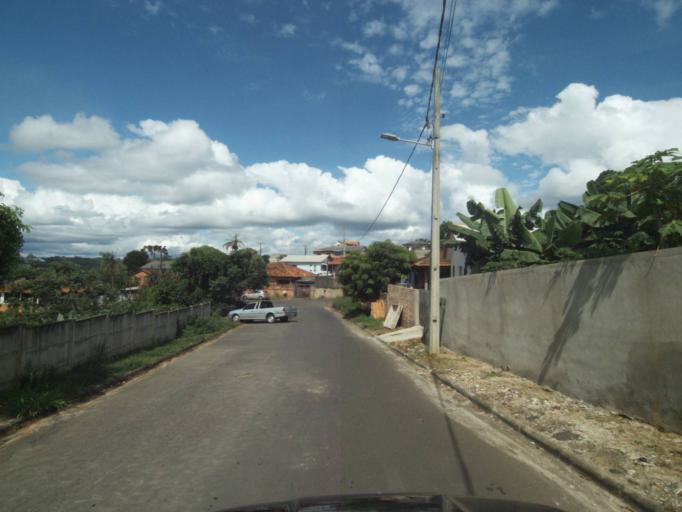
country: BR
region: Parana
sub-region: Telemaco Borba
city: Telemaco Borba
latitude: -24.3153
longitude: -50.6290
